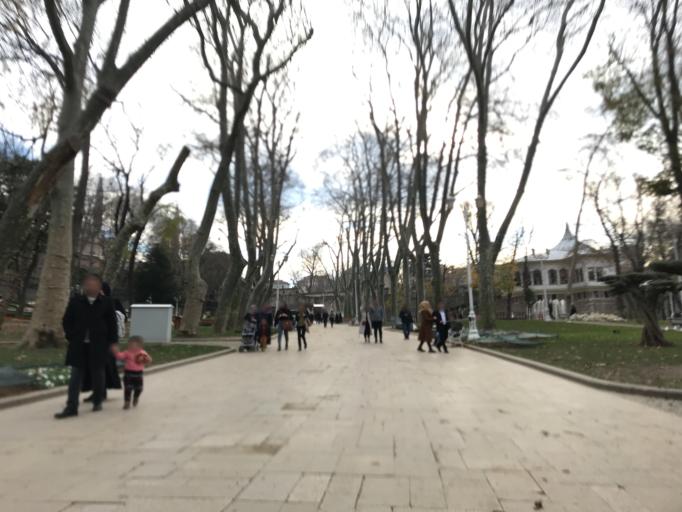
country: TR
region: Istanbul
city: Eminoenue
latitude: 41.0121
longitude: 28.9793
